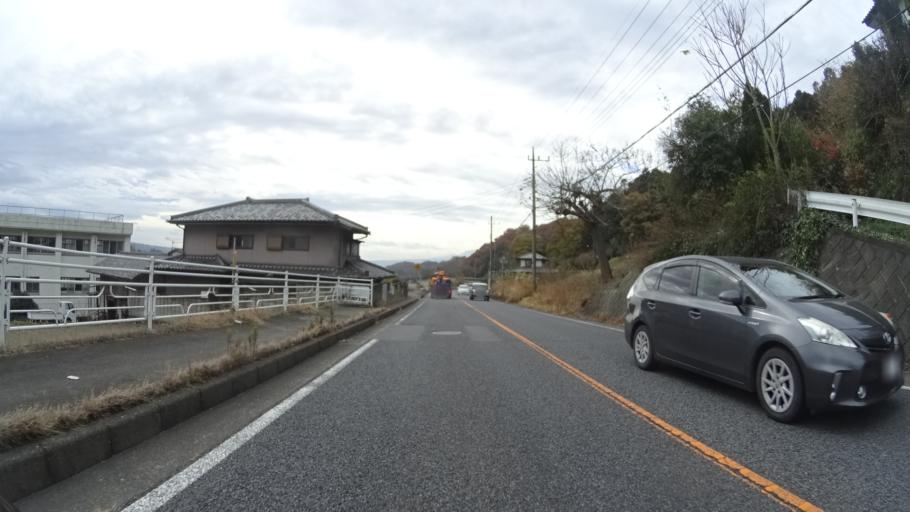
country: JP
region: Gunma
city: Numata
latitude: 36.5574
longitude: 139.0351
